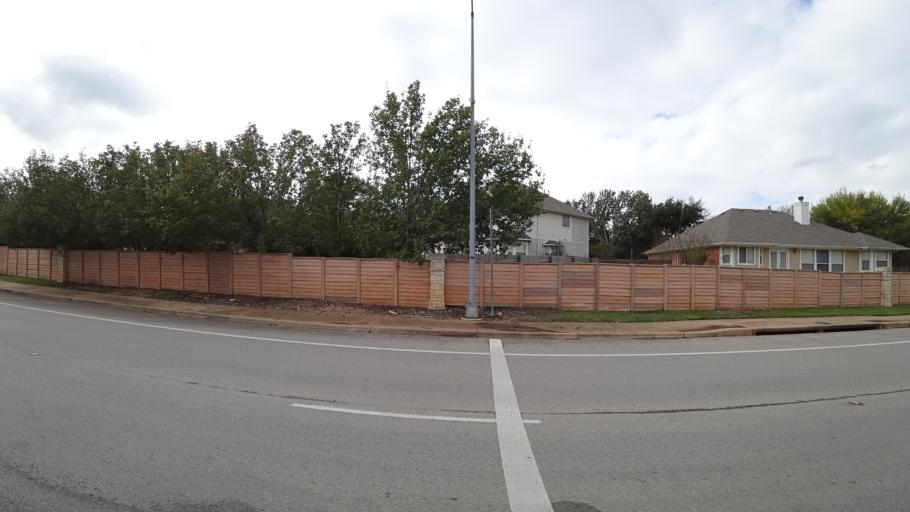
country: US
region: Texas
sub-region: Williamson County
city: Brushy Creek
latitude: 30.5159
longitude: -97.7177
